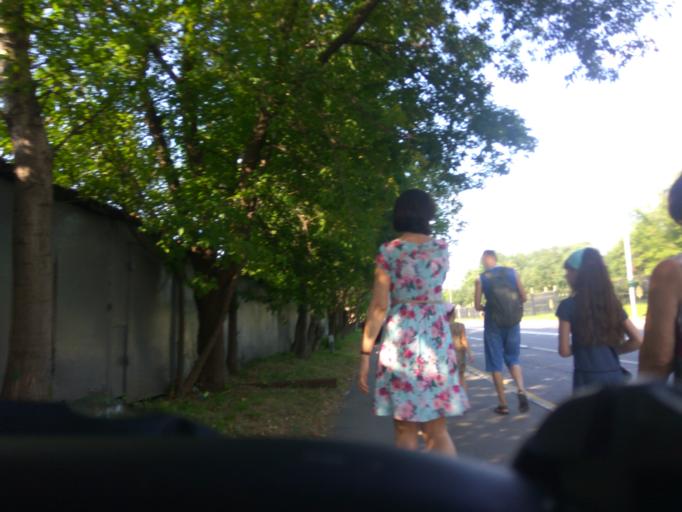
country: RU
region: Moscow
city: Orekhovo-Borisovo Severnoye
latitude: 55.6201
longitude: 37.6734
